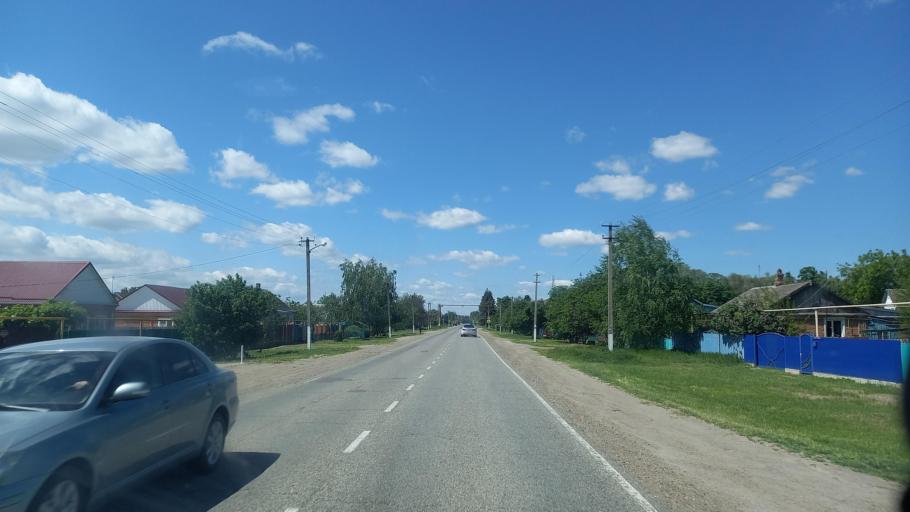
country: RU
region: Krasnodarskiy
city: Kazanskaya
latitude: 45.3630
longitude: 40.3873
